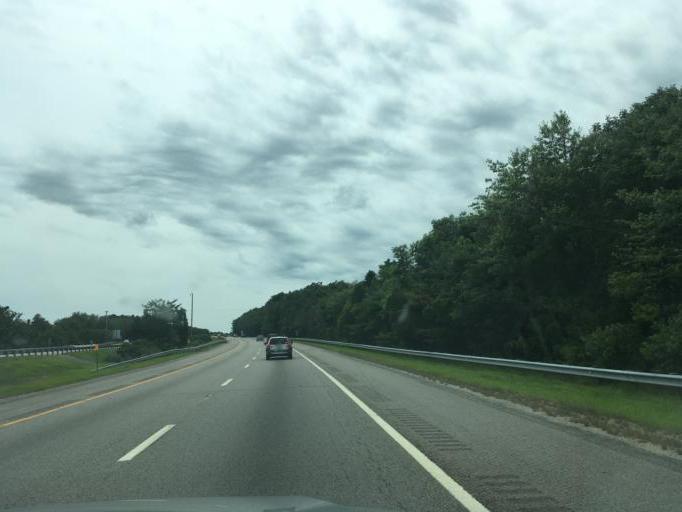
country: US
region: Rhode Island
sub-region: Kent County
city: West Greenwich
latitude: 41.6411
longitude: -71.6242
